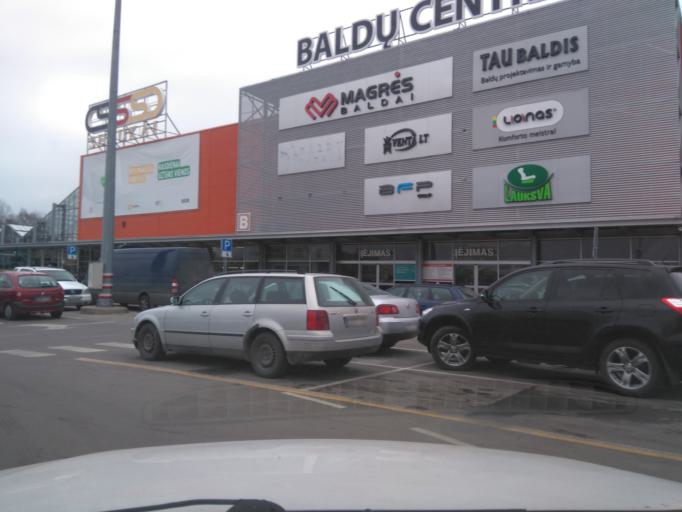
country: LT
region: Kauno apskritis
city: Dainava (Kaunas)
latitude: 54.9083
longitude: 23.9877
